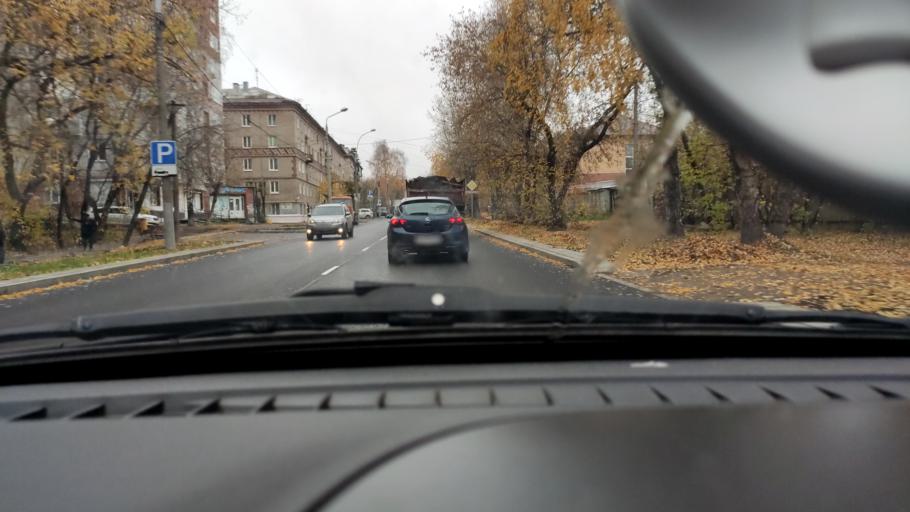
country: RU
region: Perm
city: Kondratovo
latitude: 58.0222
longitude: 56.0127
